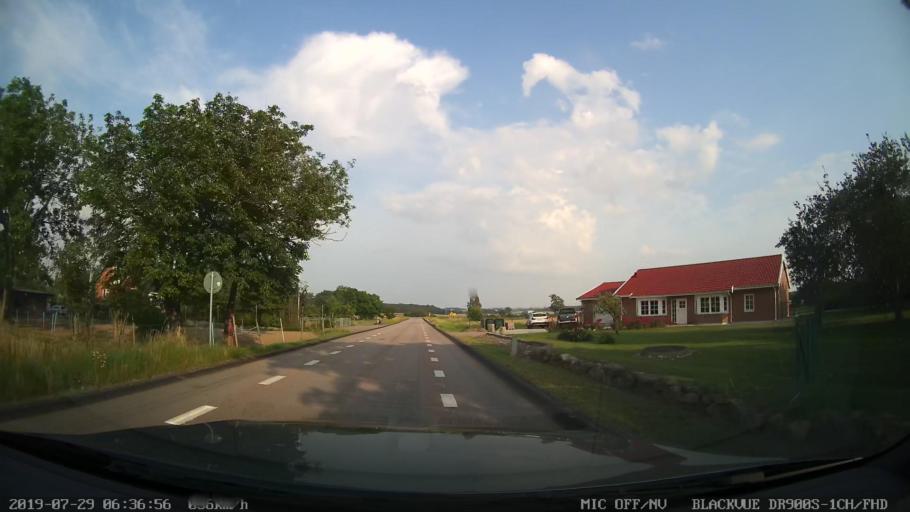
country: SE
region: Skane
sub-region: Helsingborg
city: Odakra
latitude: 56.1072
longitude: 12.7158
